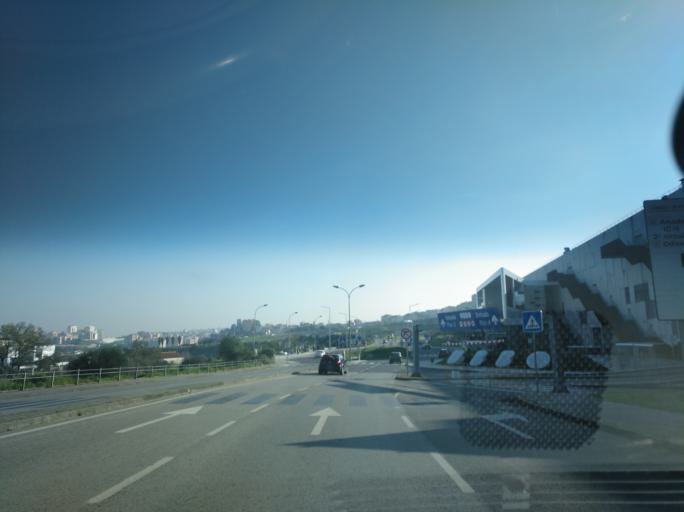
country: PT
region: Lisbon
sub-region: Odivelas
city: Famoes
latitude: 38.7781
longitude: -9.2181
